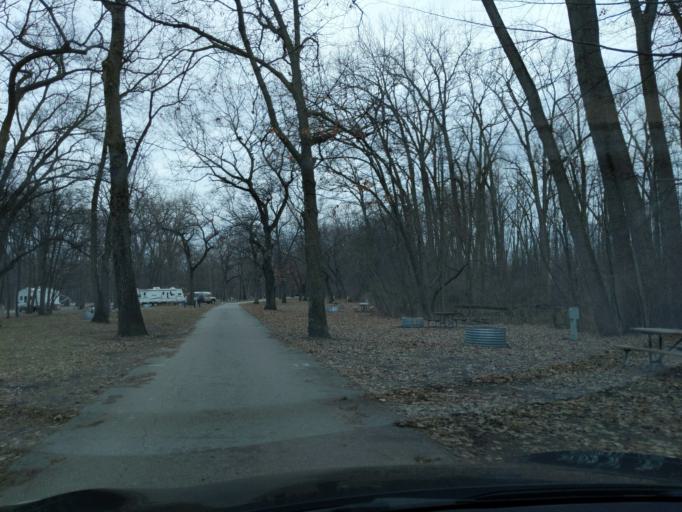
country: US
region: Michigan
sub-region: Bay County
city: Bay City
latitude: 43.6643
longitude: -83.9033
